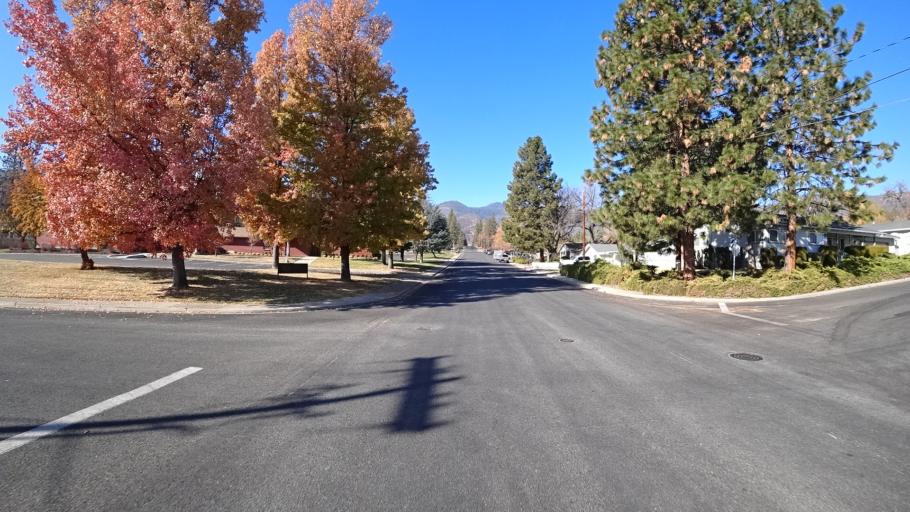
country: US
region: California
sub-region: Siskiyou County
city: Yreka
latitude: 41.7348
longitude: -122.6510
